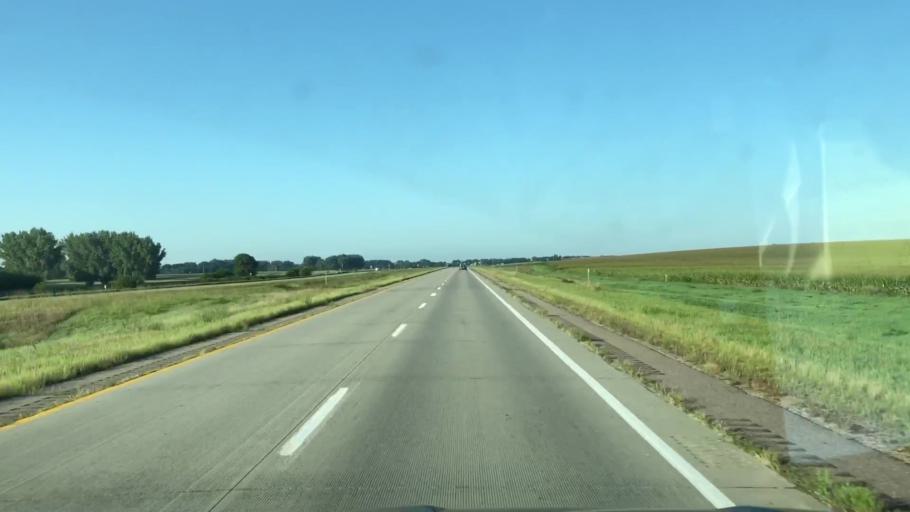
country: US
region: Iowa
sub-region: Plymouth County
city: Le Mars
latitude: 42.8732
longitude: -96.1087
